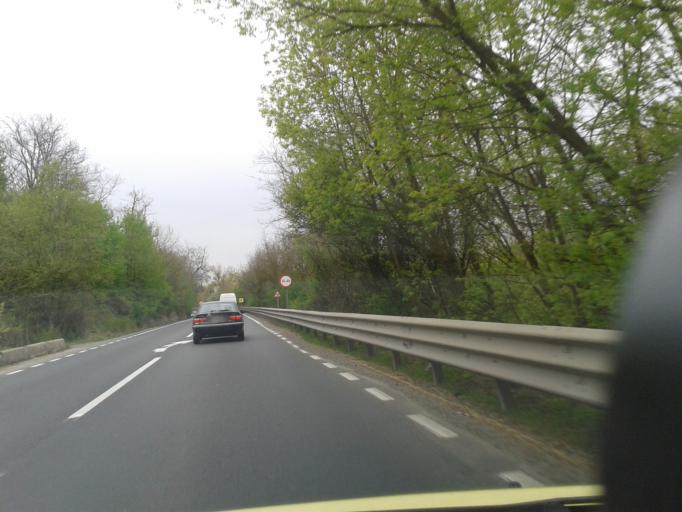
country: RO
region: Arad
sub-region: Comuna Bata
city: Bata
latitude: 46.0413
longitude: 22.0596
